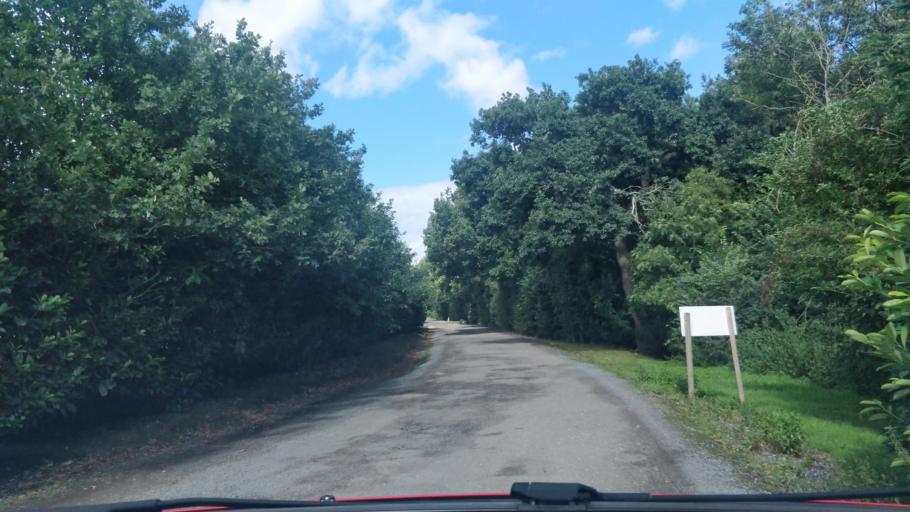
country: GB
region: Wales
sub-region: Wrexham
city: Rossett
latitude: 53.1491
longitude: -2.9344
